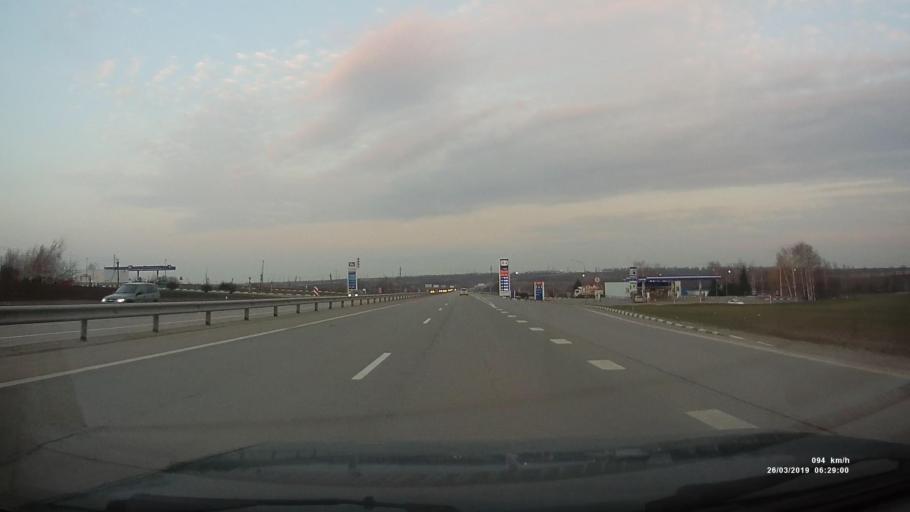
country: RU
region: Rostov
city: Kalinin
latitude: 47.2663
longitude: 39.5824
